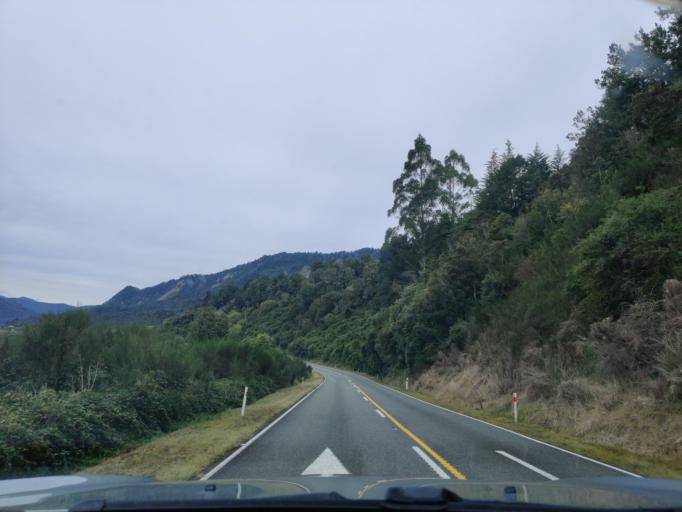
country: NZ
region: West Coast
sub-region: Buller District
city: Westport
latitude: -41.8595
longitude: 171.8647
